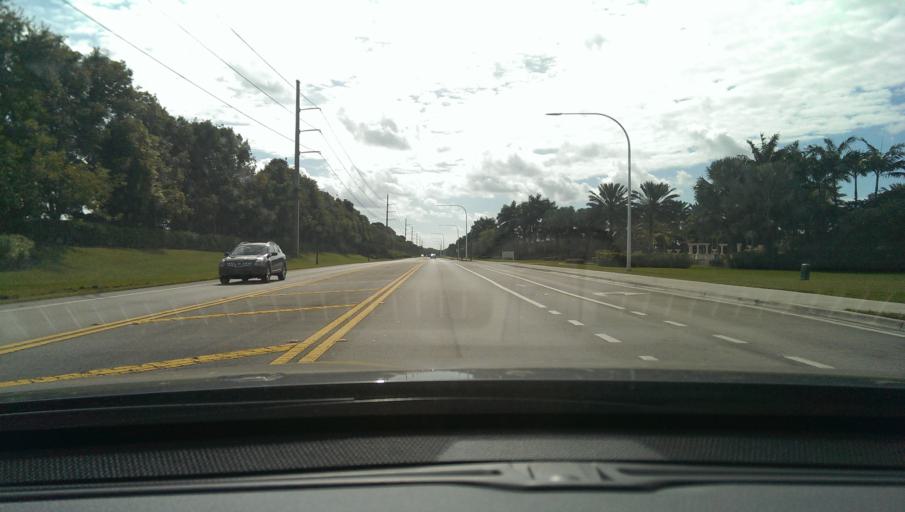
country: US
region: Florida
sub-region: Broward County
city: Weston
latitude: 26.0831
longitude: -80.4040
